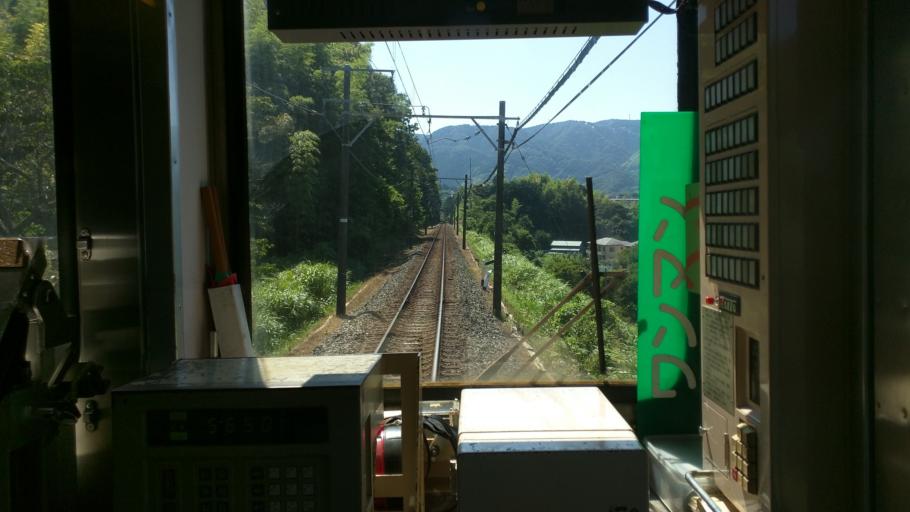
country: JP
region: Shizuoka
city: Ito
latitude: 34.9507
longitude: 139.1029
